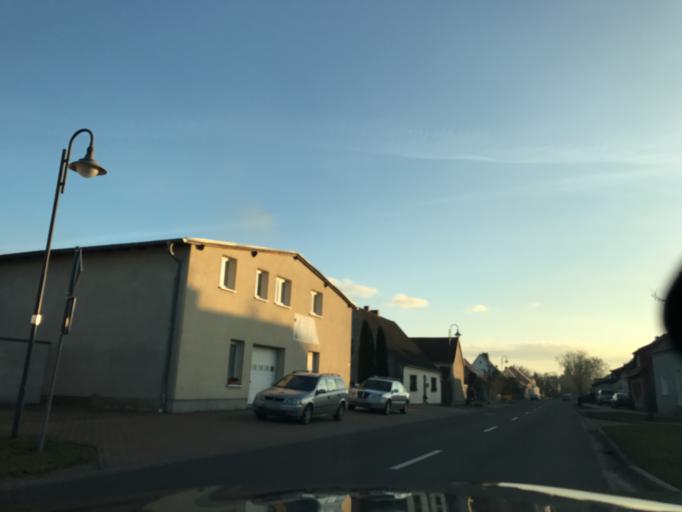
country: DE
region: Saxony-Anhalt
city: Genthin
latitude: 52.4267
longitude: 12.2075
